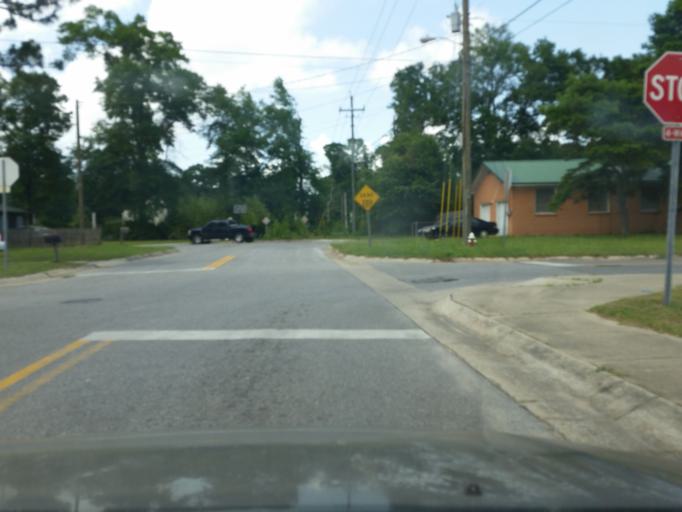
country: US
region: Florida
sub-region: Escambia County
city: Ferry Pass
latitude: 30.5016
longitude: -87.1963
